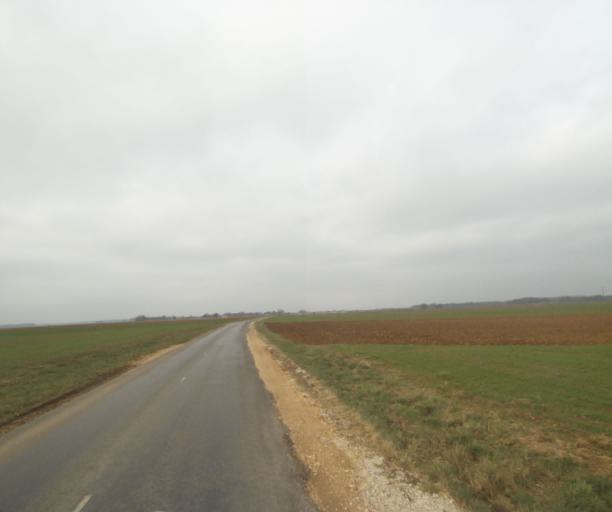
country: FR
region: Champagne-Ardenne
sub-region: Departement de la Haute-Marne
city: Villiers-en-Lieu
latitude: 48.6774
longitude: 4.8558
